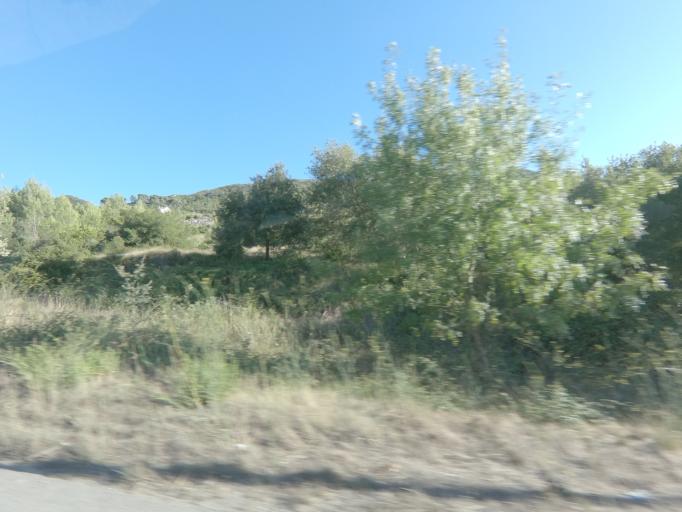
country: PT
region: Setubal
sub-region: Palmela
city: Quinta do Anjo
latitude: 38.5038
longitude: -8.9660
